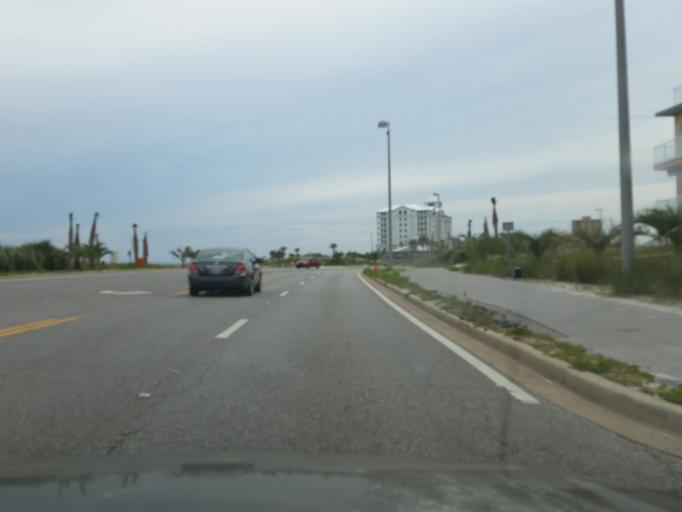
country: US
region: Florida
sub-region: Santa Rosa County
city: Gulf Breeze
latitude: 30.3317
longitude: -87.1435
